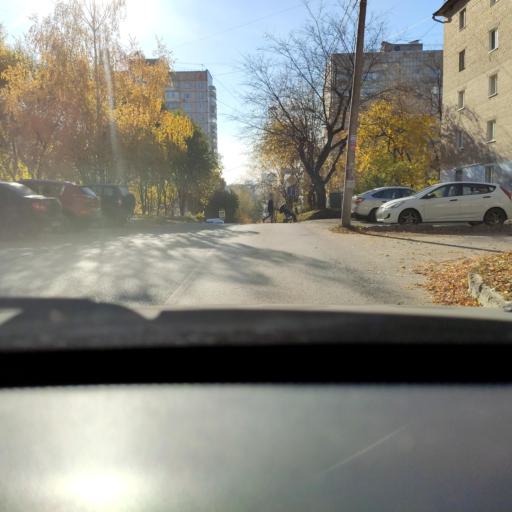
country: RU
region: Perm
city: Perm
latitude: 58.0090
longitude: 56.2038
